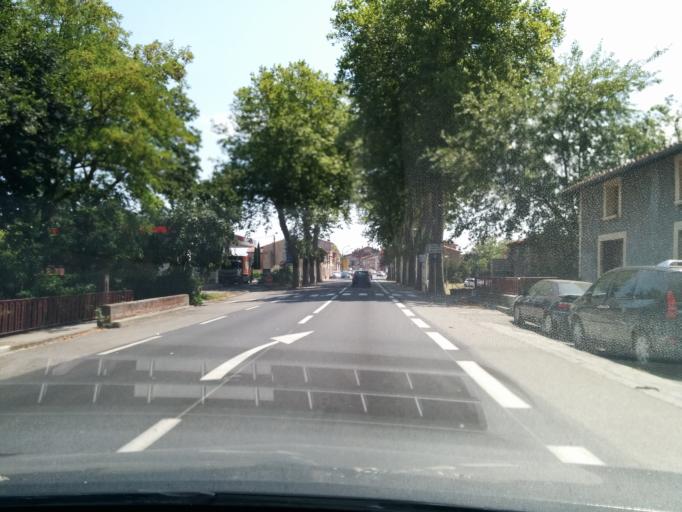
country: FR
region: Midi-Pyrenees
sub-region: Departement de la Haute-Garonne
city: Villefranche-de-Lauragais
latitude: 43.4033
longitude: 1.7117
